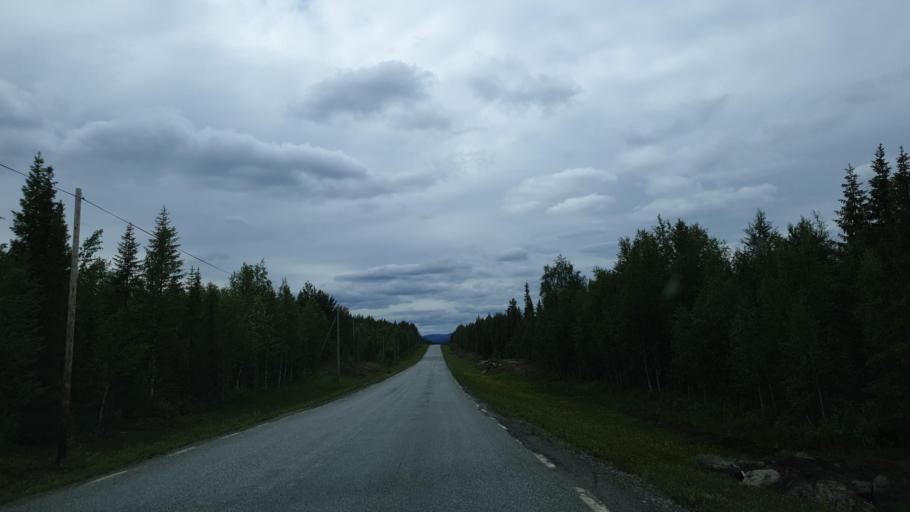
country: SE
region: Vaesterbotten
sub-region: Vilhelmina Kommun
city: Sjoberg
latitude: 65.4185
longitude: 16.1378
